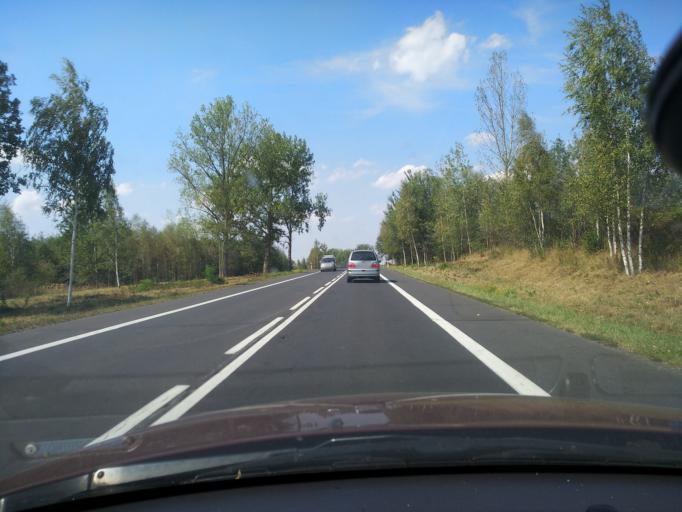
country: PL
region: Lower Silesian Voivodeship
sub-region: Powiat lubanski
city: Luban
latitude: 51.0927
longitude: 15.3194
